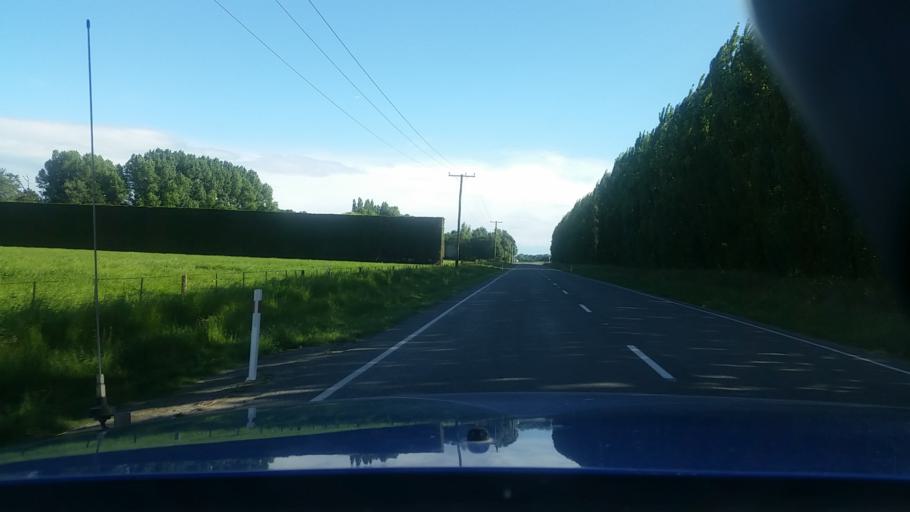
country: NZ
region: Canterbury
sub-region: Ashburton District
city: Ashburton
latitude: -43.8601
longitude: 171.7305
